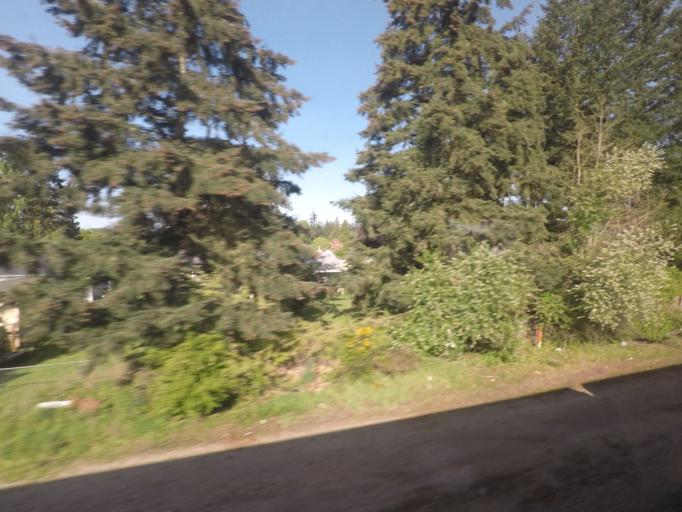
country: US
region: Washington
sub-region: Snohomish County
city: Smokey Point
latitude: 48.1030
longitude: -122.1767
